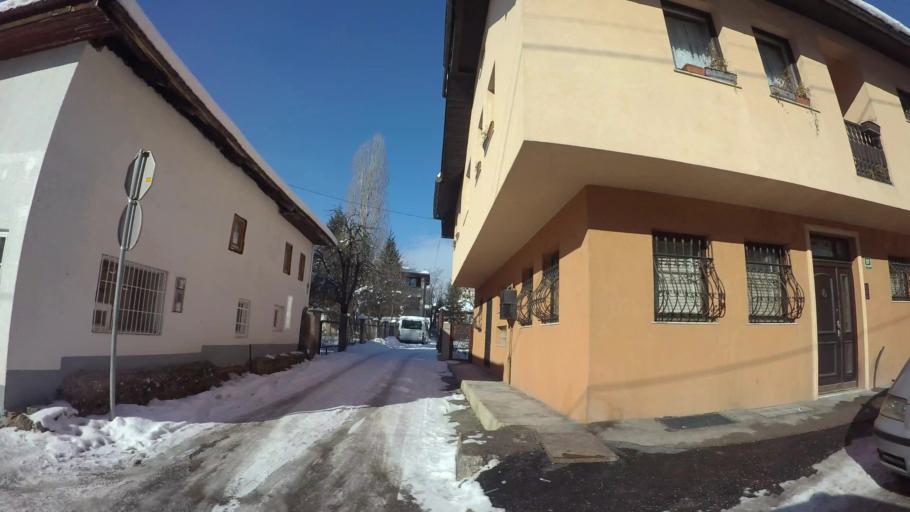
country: BA
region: Federation of Bosnia and Herzegovina
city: Kobilja Glava
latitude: 43.8644
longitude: 18.4191
